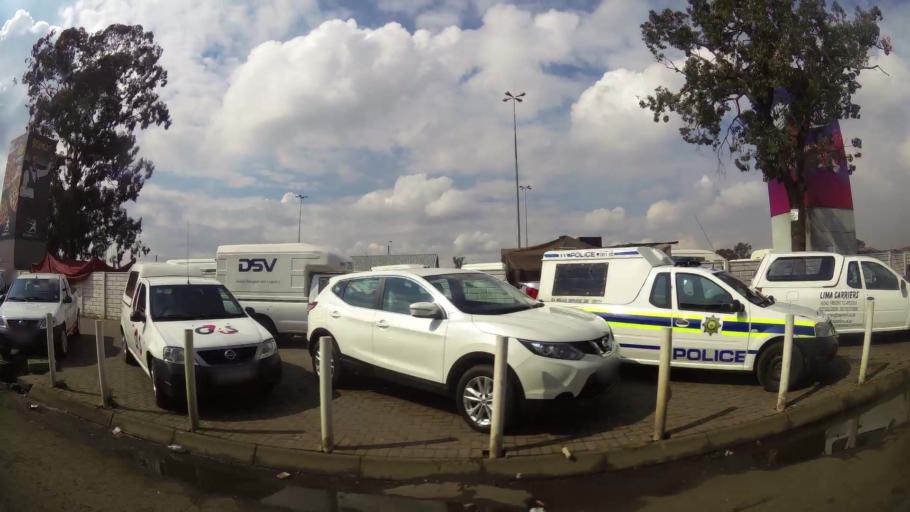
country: ZA
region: Gauteng
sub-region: Sedibeng District Municipality
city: Vereeniging
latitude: -26.6723
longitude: 27.9344
